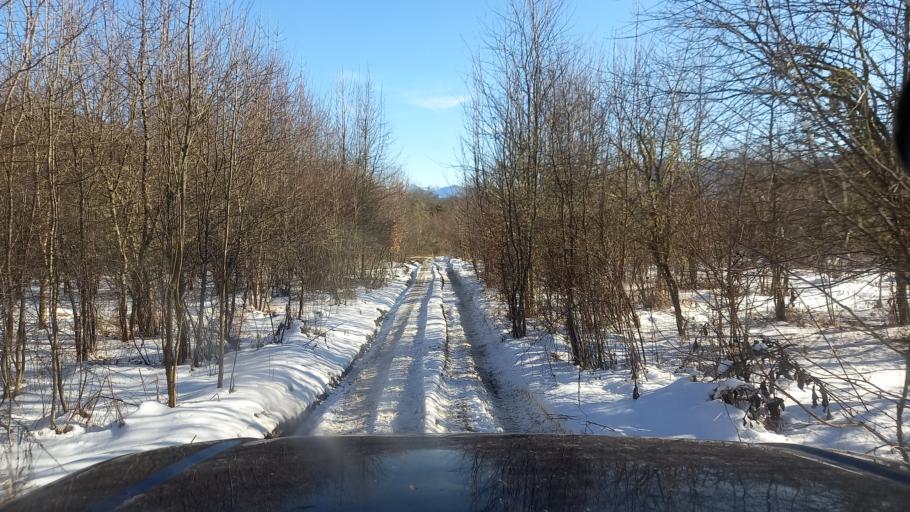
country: RU
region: Adygeya
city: Kamennomostskiy
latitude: 44.2100
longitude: 40.1443
